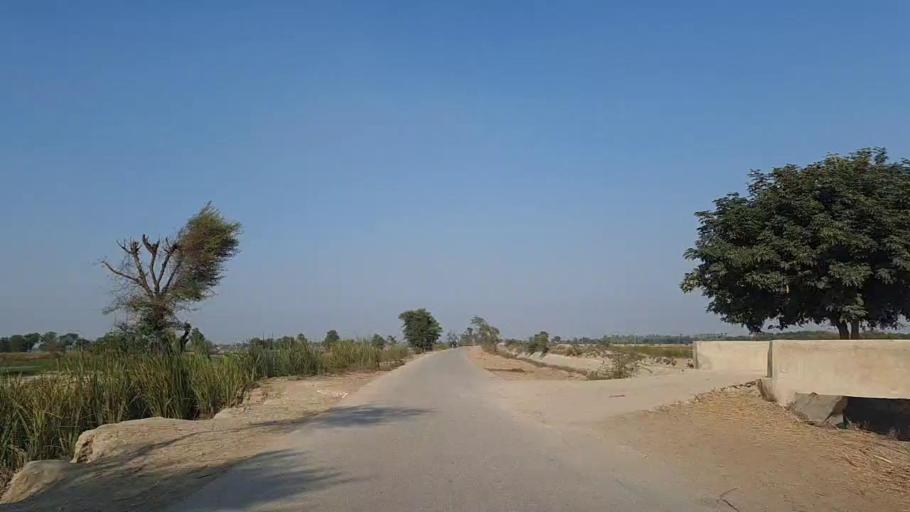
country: PK
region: Sindh
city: Daur
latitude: 26.4260
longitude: 68.2629
